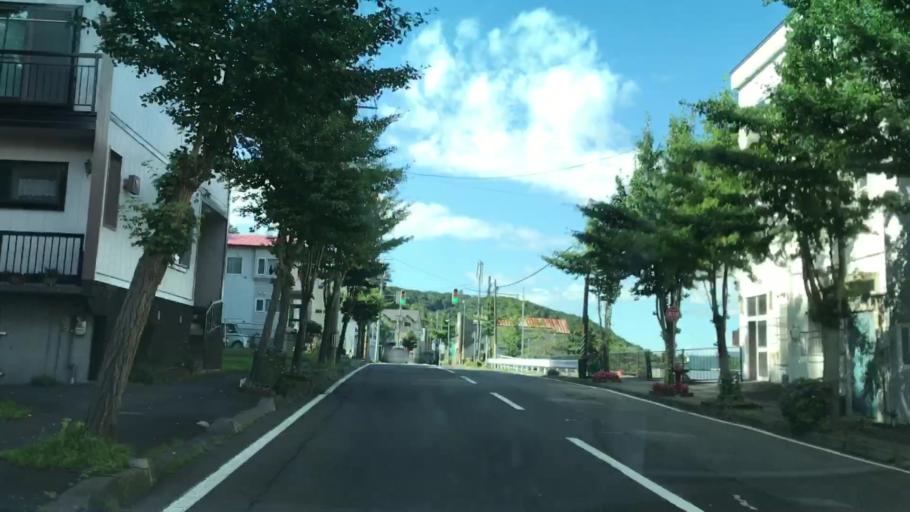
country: JP
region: Hokkaido
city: Muroran
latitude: 42.3210
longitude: 140.9701
